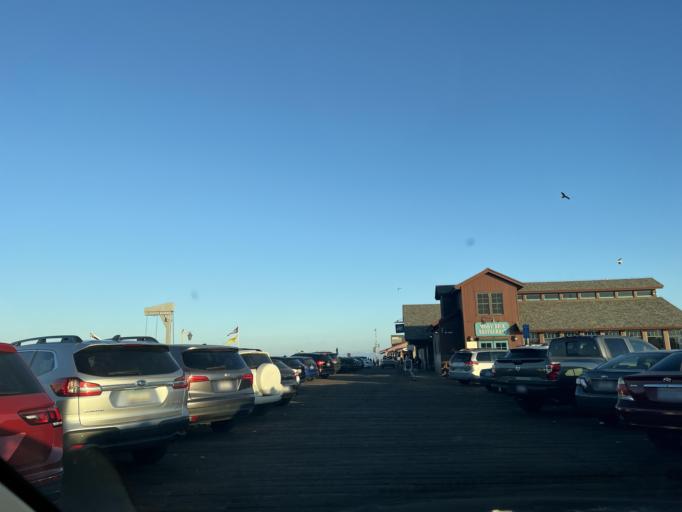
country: US
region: California
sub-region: Santa Barbara County
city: Santa Barbara
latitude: 34.4097
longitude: -119.6854
